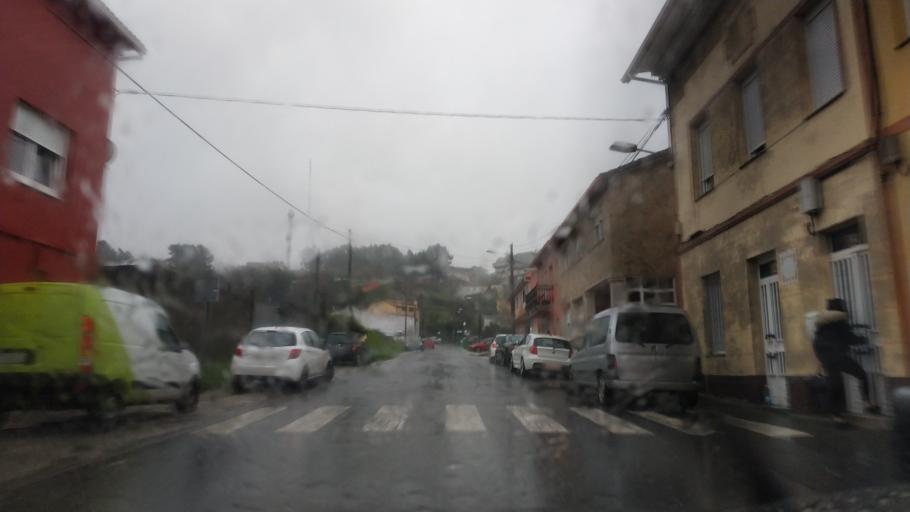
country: ES
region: Galicia
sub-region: Provincia da Coruna
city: A Coruna
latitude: 43.3311
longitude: -8.4088
